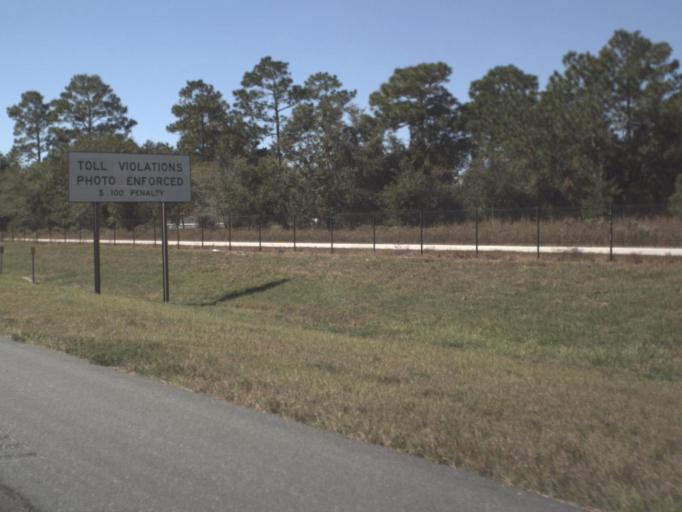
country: US
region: Florida
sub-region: Pasco County
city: Shady Hills
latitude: 28.4111
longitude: -82.5045
